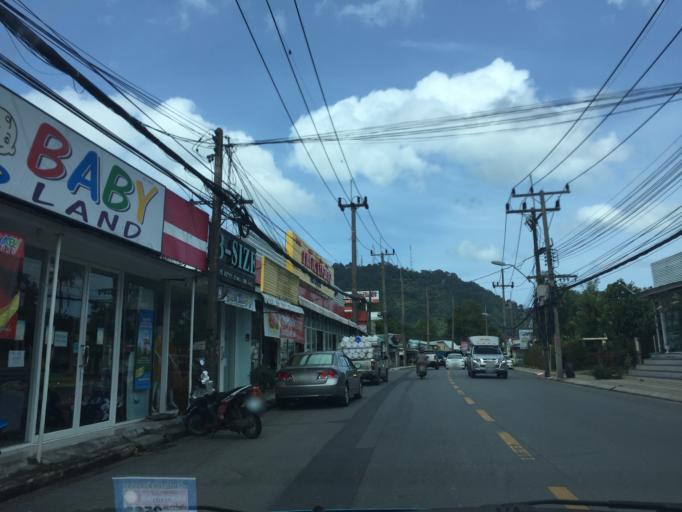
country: TH
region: Phuket
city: Wichit
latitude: 7.9020
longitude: 98.3796
